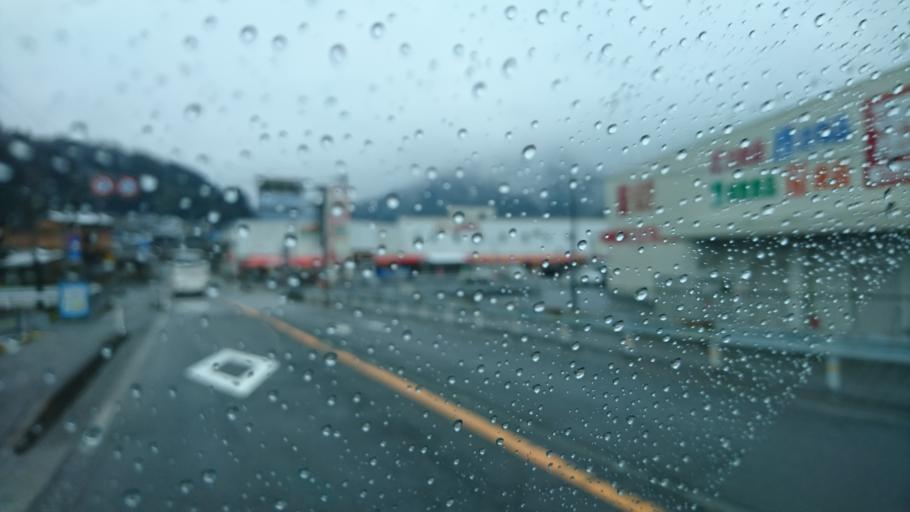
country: JP
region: Tottori
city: Tottori
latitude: 35.5658
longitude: 134.4828
